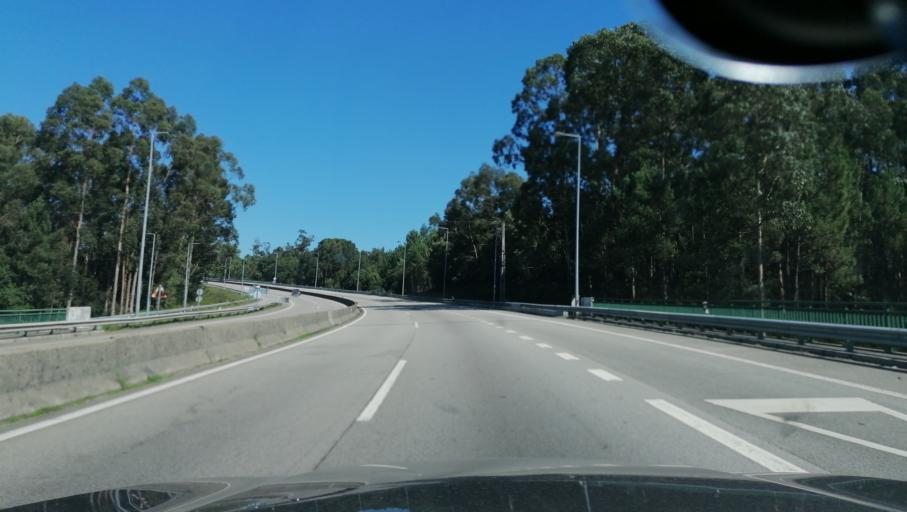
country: PT
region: Aveiro
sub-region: Santa Maria da Feira
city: Rio Meao
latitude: 40.9243
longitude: -8.5798
